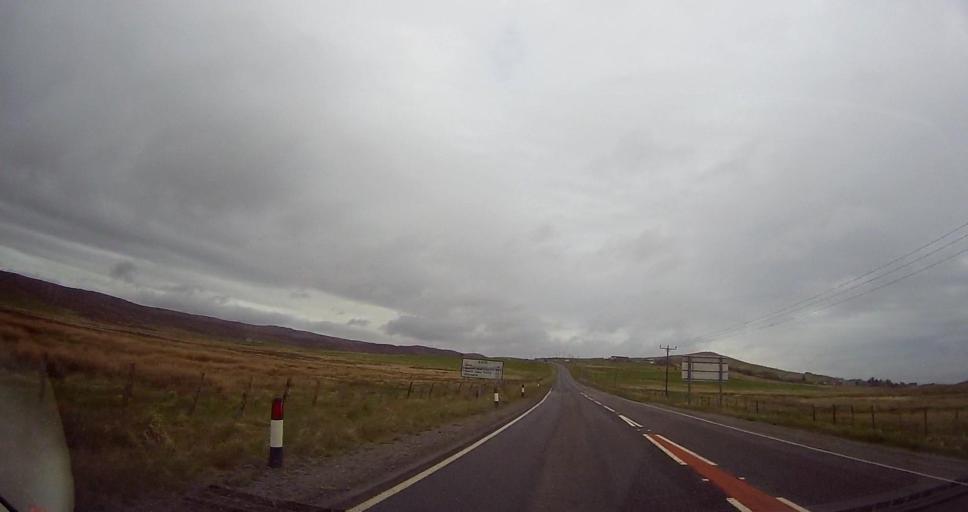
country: GB
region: Scotland
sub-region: Shetland Islands
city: Lerwick
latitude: 60.1920
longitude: -1.2320
